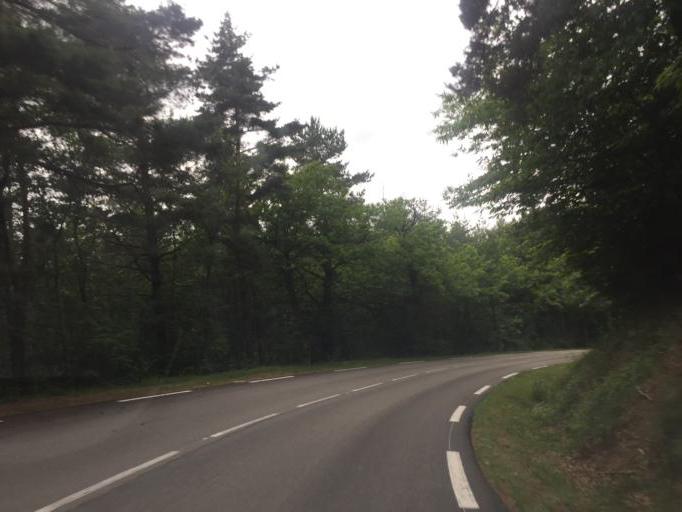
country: FR
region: Rhone-Alpes
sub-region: Departement de l'Ardeche
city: Privas
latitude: 44.7657
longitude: 4.5851
